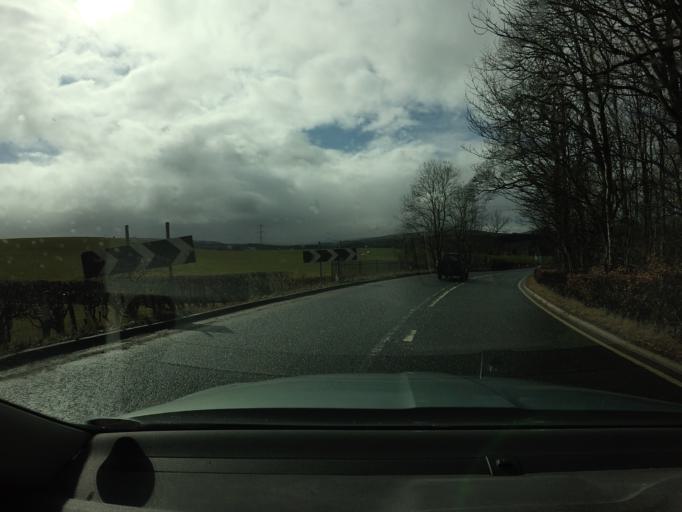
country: GB
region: Scotland
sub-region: South Lanarkshire
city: Douglas
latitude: 55.5896
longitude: -3.7968
